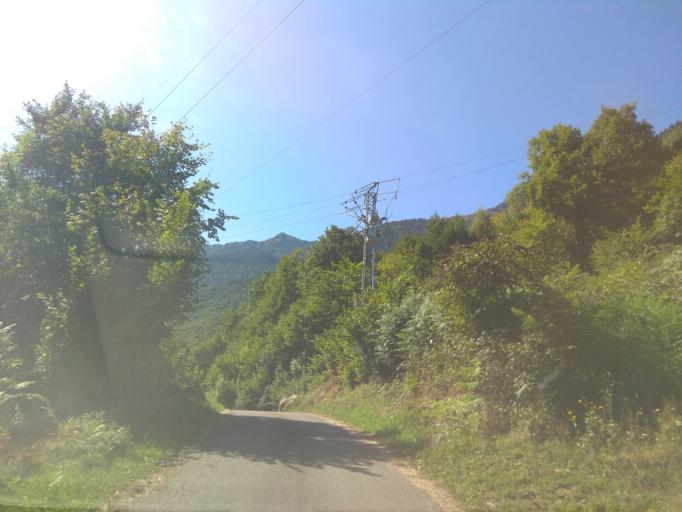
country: ES
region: Catalonia
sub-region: Provincia de Lleida
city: Les
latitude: 42.7571
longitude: 0.6938
